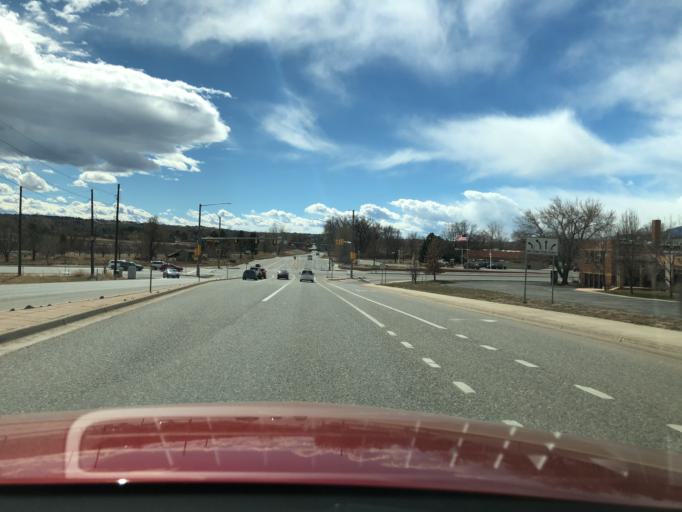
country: US
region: Colorado
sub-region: Boulder County
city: Gunbarrel
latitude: 40.0159
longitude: -105.1782
